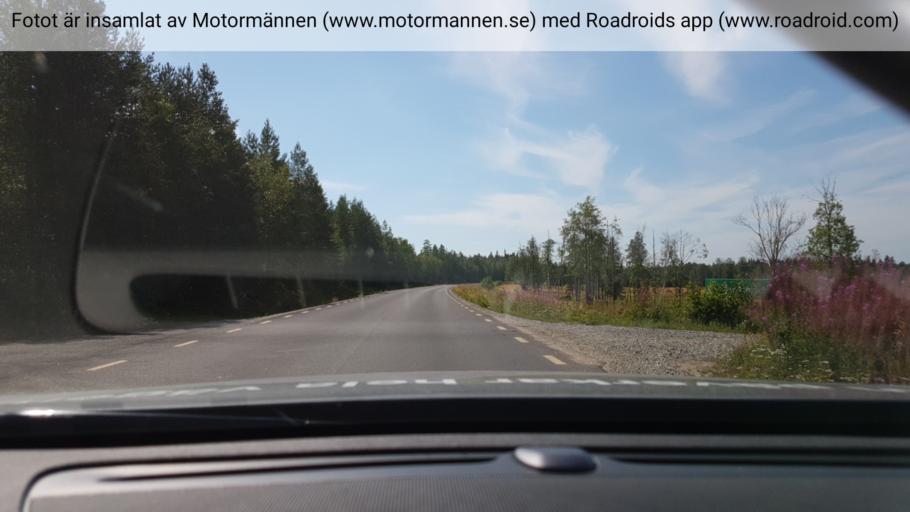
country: SE
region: Vaesterbotten
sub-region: Norsjo Kommun
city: Norsjoe
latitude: 64.5158
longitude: 19.3456
